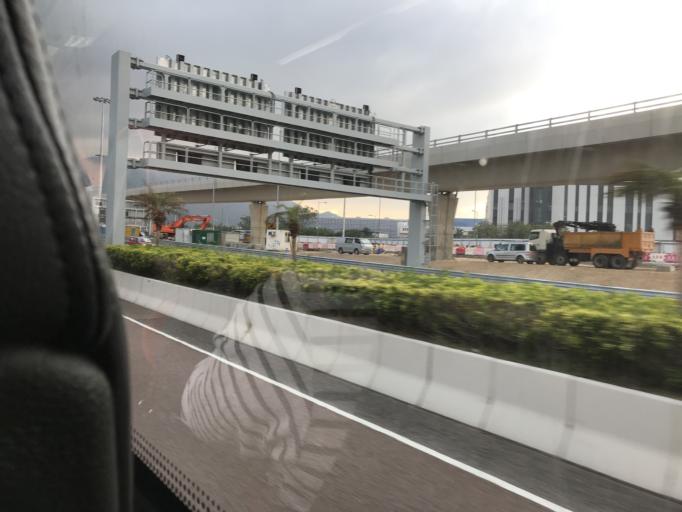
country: HK
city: Tai O
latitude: 22.3030
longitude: 113.9361
